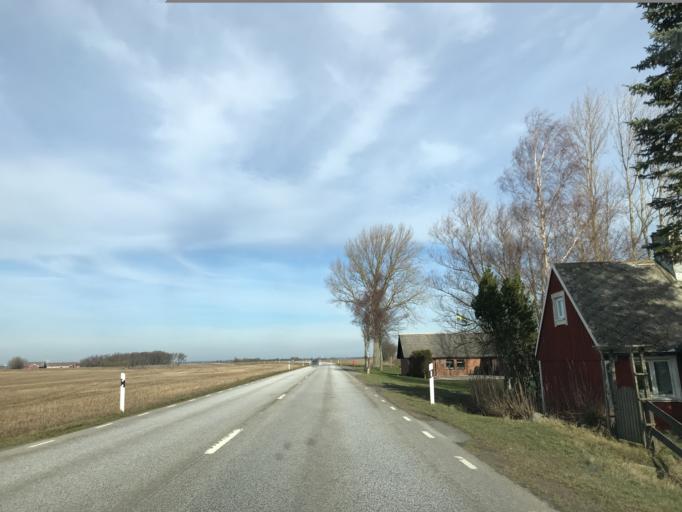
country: SE
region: Skane
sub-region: Tomelilla Kommun
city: Tomelilla
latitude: 55.5325
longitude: 13.9119
